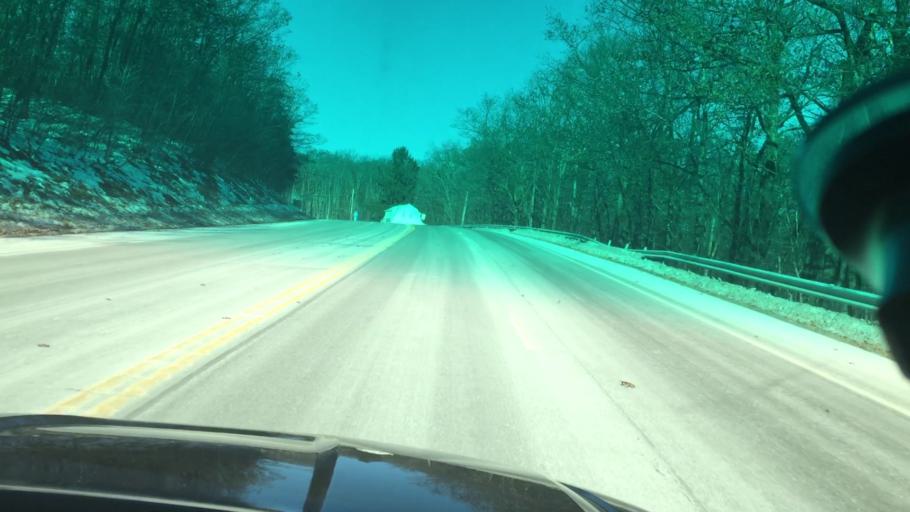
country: US
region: Pennsylvania
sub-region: Luzerne County
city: Freeland
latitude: 41.0716
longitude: -75.9583
